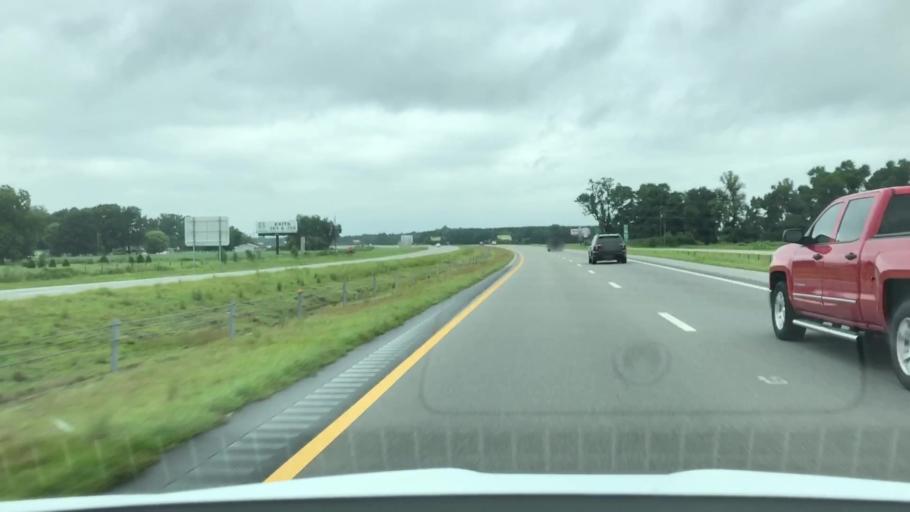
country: US
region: North Carolina
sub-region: Wayne County
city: Elroy
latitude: 35.3878
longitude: -77.8654
